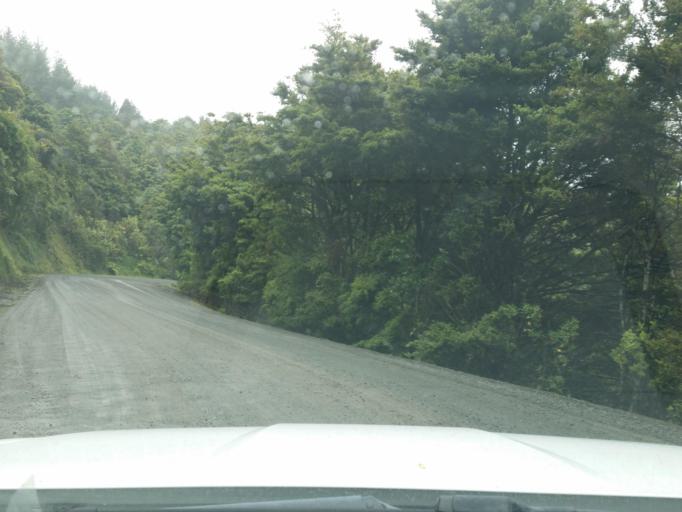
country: NZ
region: Northland
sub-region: Kaipara District
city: Dargaville
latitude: -35.7350
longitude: 173.9072
